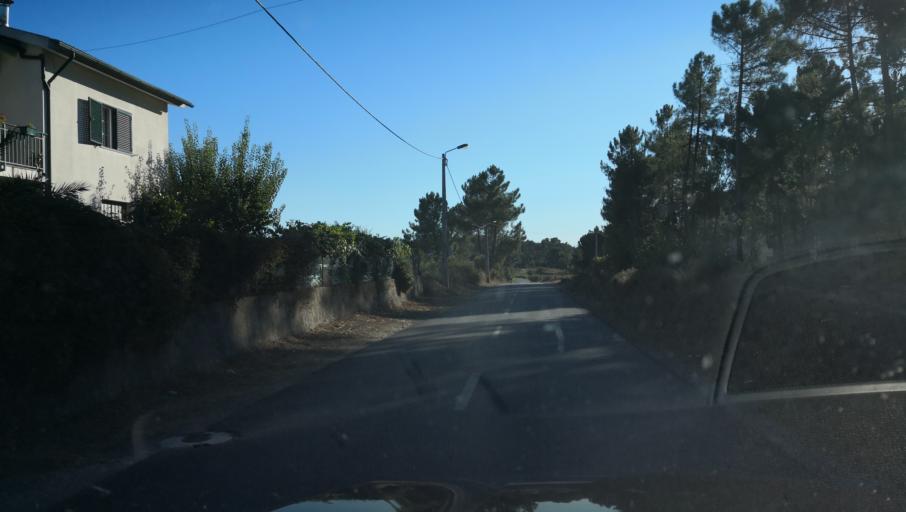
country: PT
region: Vila Real
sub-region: Vila Real
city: Vila Real
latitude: 41.2732
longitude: -7.7269
